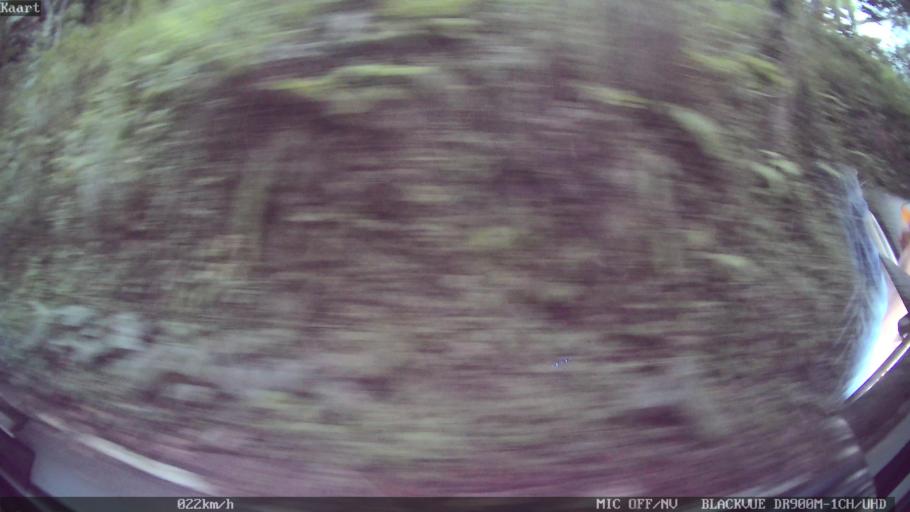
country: ID
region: Bali
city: Peneng
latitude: -8.3697
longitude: 115.2150
